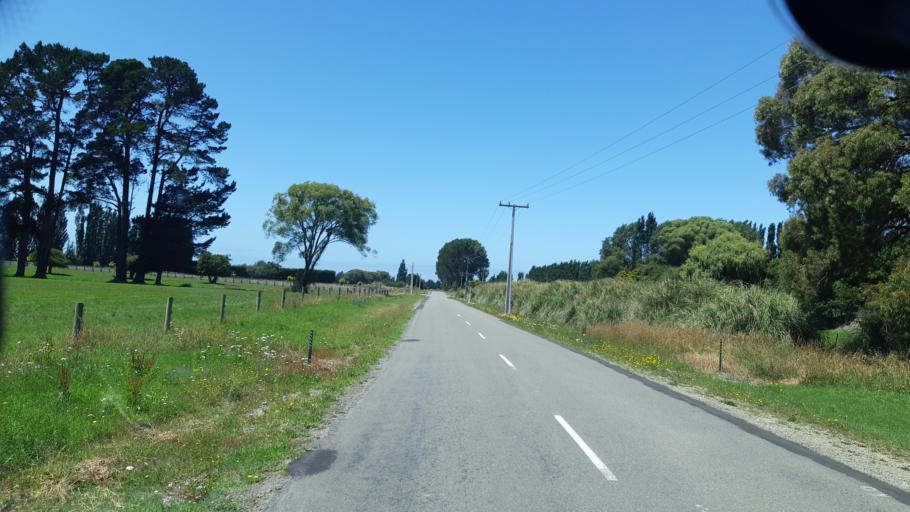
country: NZ
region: Canterbury
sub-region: Waimakariri District
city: Woodend
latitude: -43.2850
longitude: 172.6761
